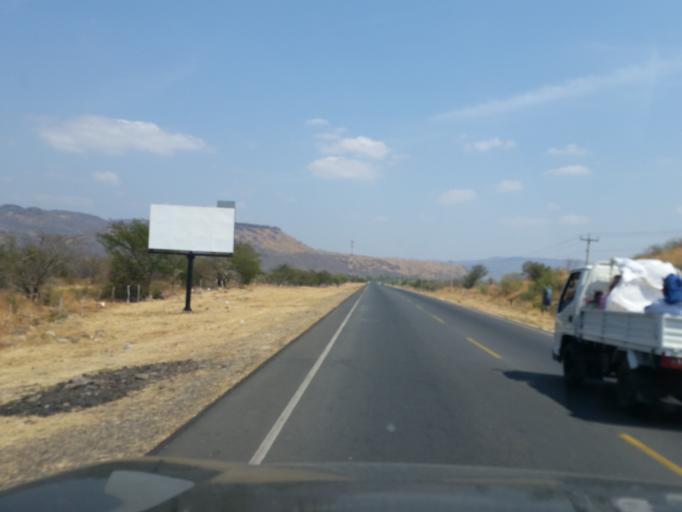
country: NI
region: Managua
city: Tipitapa
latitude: 12.4259
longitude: -86.0418
